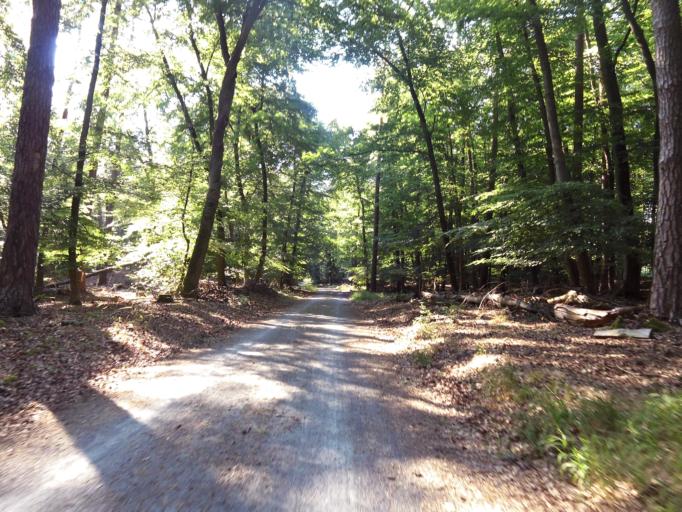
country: DE
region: Hesse
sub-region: Regierungsbezirk Darmstadt
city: Nauheim
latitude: 49.9713
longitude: 8.5164
